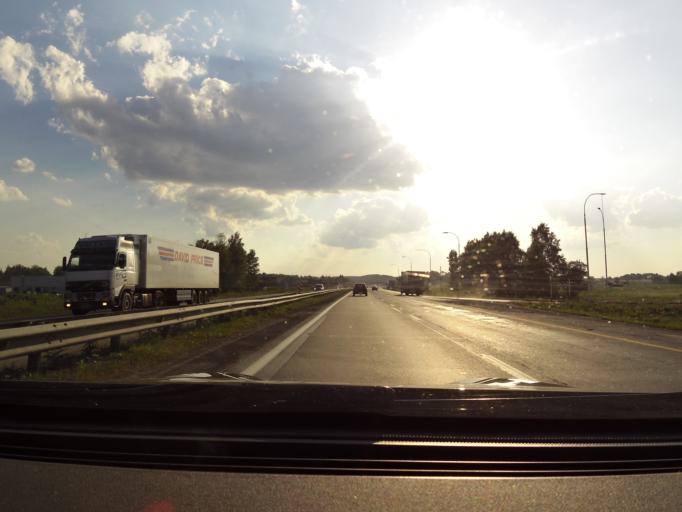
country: RU
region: Sverdlovsk
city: Talitsa
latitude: 56.8378
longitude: 60.1598
